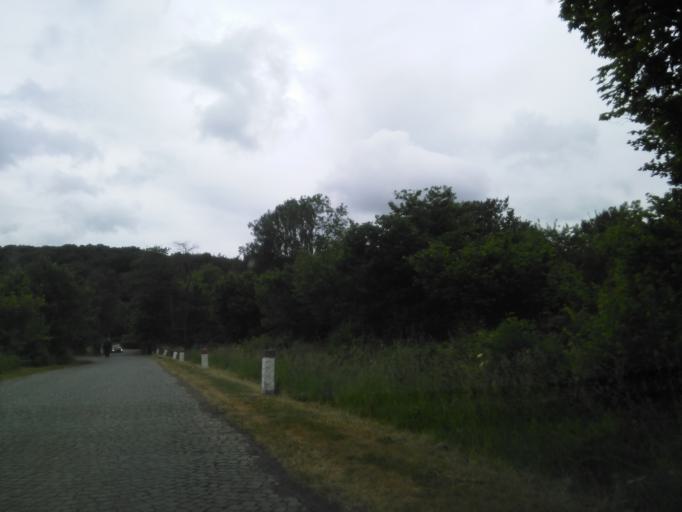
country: DK
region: Capital Region
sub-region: Bornholm Kommune
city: Akirkeby
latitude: 55.1106
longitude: 14.9085
